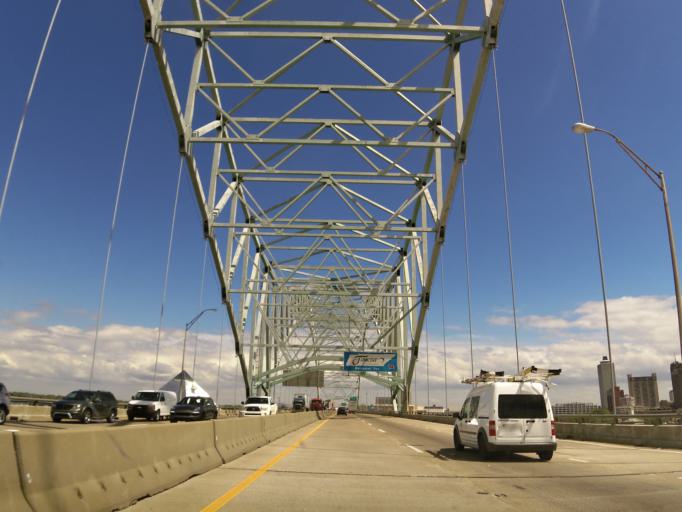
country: US
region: Tennessee
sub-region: Shelby County
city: Memphis
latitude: 35.1531
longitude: -90.0630
